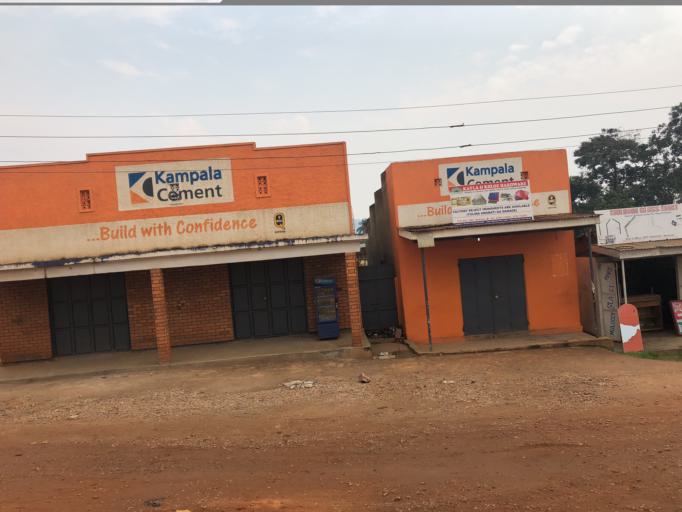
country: UG
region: Central Region
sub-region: Mukono District
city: Mukono
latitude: 0.3519
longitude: 32.7595
